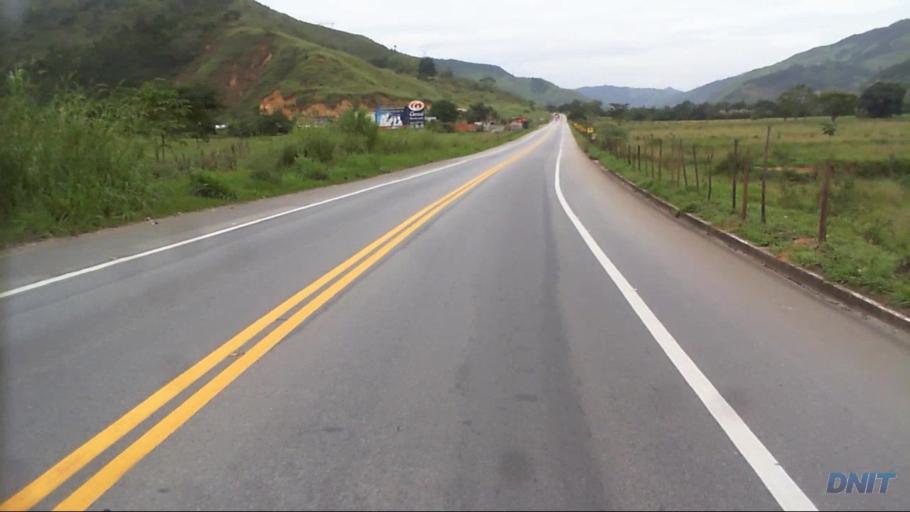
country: BR
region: Minas Gerais
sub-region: Timoteo
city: Timoteo
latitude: -19.5844
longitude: -42.7291
